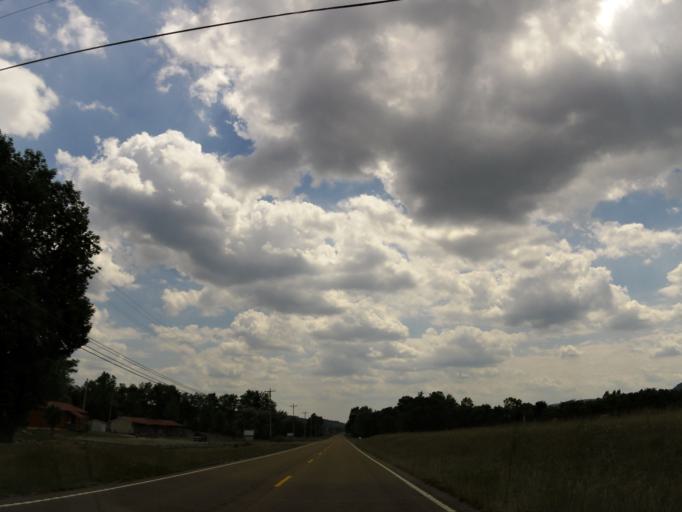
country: US
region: Tennessee
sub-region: Bledsoe County
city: Pikeville
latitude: 35.5223
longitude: -85.2755
